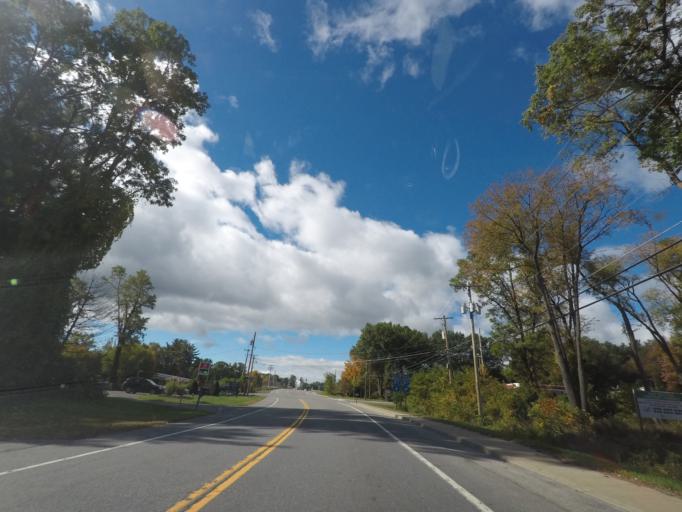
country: US
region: New York
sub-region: Saratoga County
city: Country Knolls
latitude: 42.9043
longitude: -73.7831
